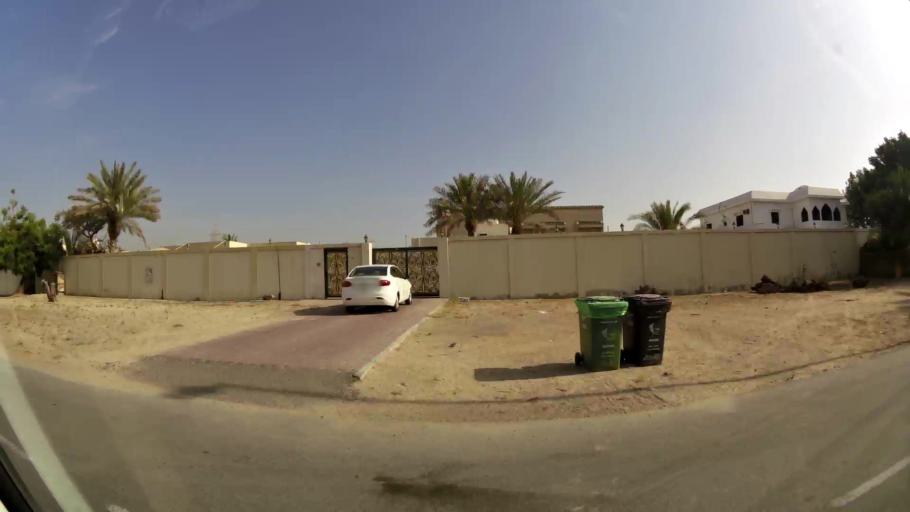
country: AE
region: Ash Shariqah
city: Sharjah
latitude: 25.2500
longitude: 55.4088
